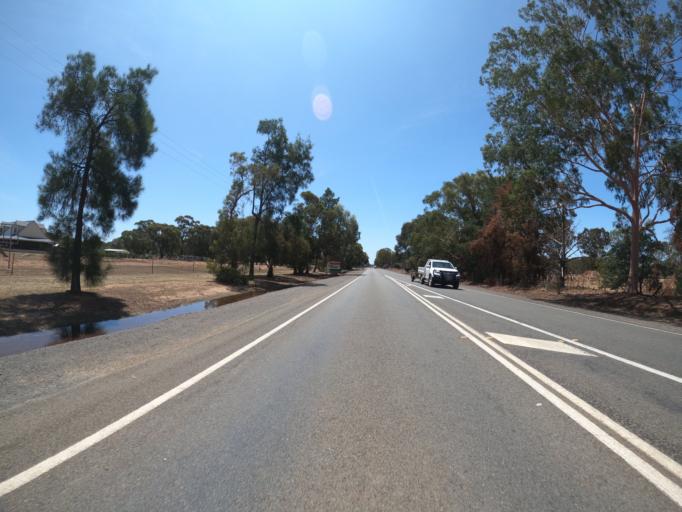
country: AU
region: Victoria
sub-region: Moira
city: Yarrawonga
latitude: -36.0397
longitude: 145.9954
